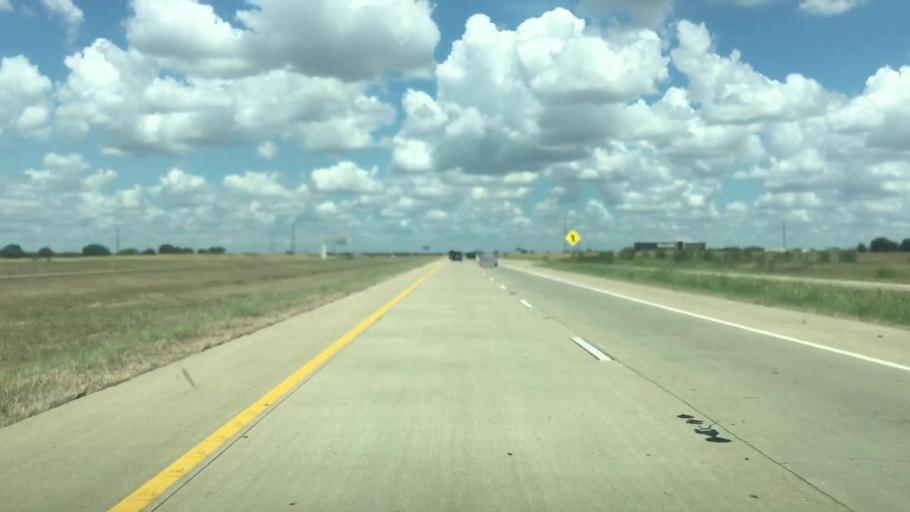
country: US
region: Texas
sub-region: Williamson County
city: Hutto
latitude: 30.5432
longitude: -97.5763
